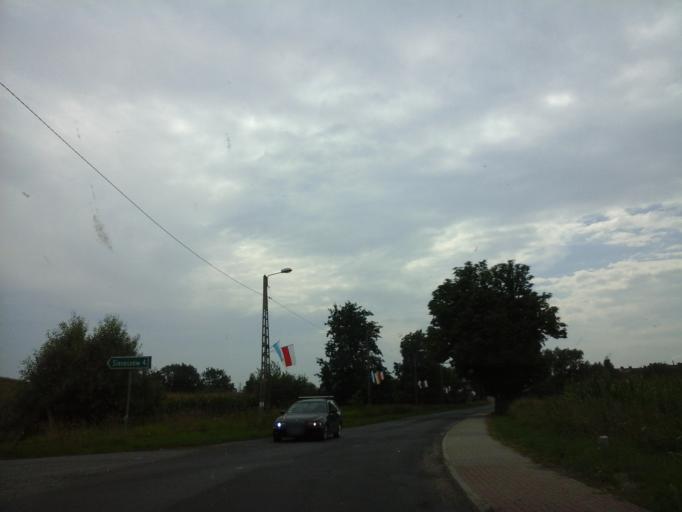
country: PL
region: Lower Silesian Voivodeship
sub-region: Powiat zabkowicki
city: Zabkowice Slaskie
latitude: 50.6220
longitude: 16.8549
